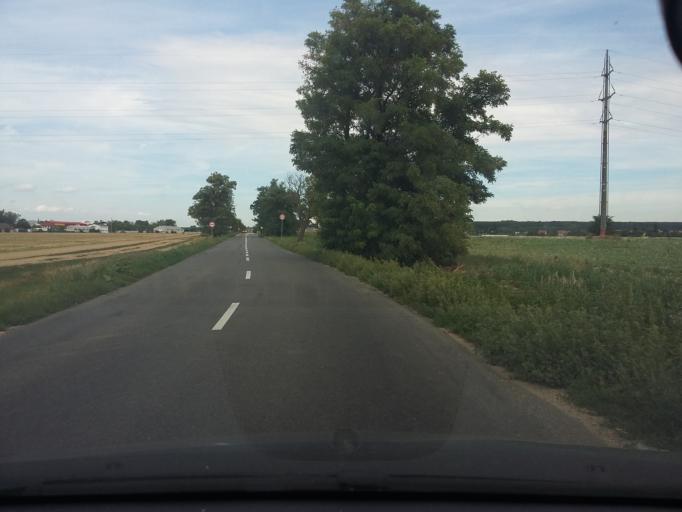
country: SK
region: Bratislavsky
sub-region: Okres Pezinok
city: Pezinok
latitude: 48.2609
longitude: 17.2975
